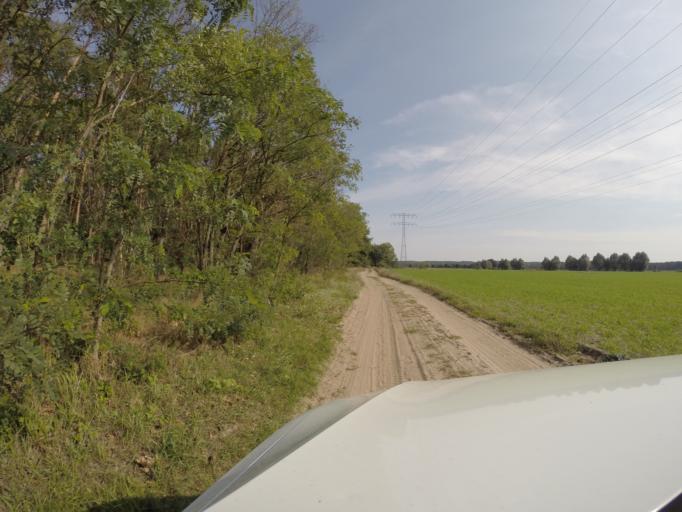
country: DE
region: Brandenburg
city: Baruth
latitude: 52.1277
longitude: 13.5042
